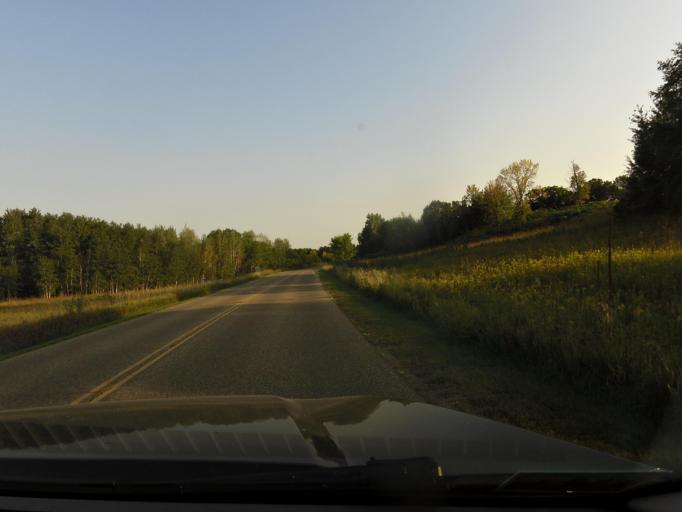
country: US
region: Minnesota
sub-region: Washington County
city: Afton
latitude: 44.8484
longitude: -92.7774
